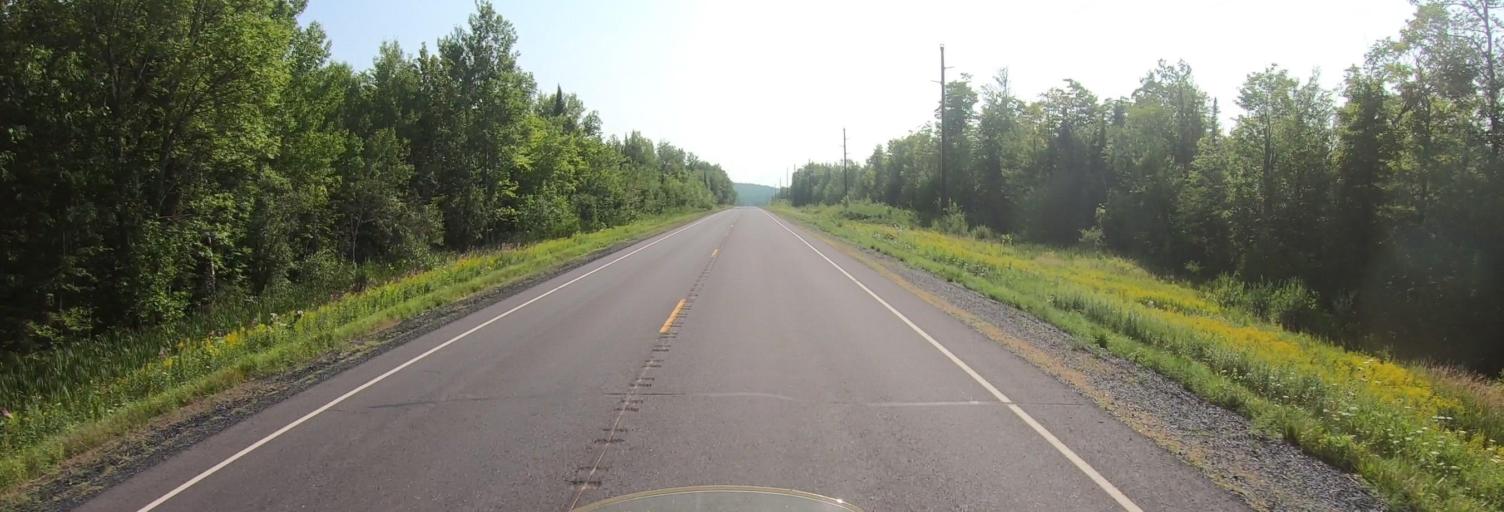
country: US
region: Wisconsin
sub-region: Iron County
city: Hurley
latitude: 46.3872
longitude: -90.3578
